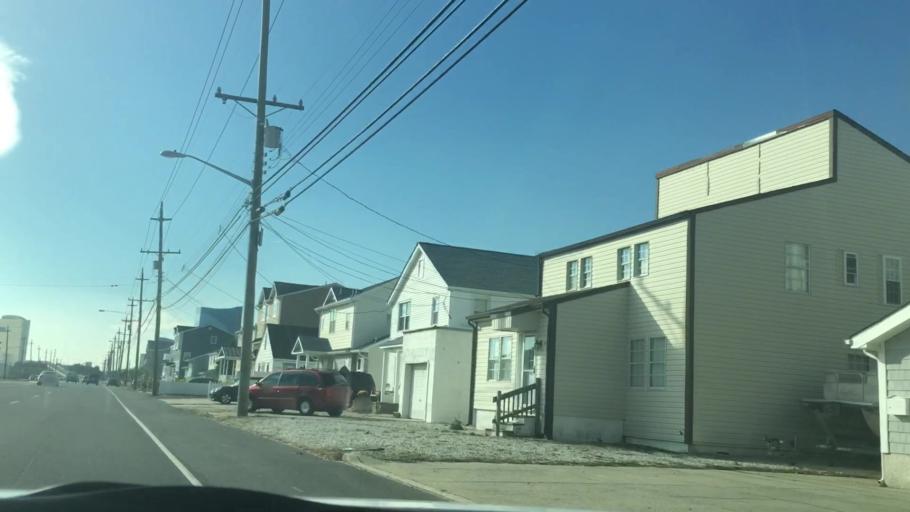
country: US
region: New Jersey
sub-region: Atlantic County
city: Atlantic City
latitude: 39.3913
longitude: -74.4102
